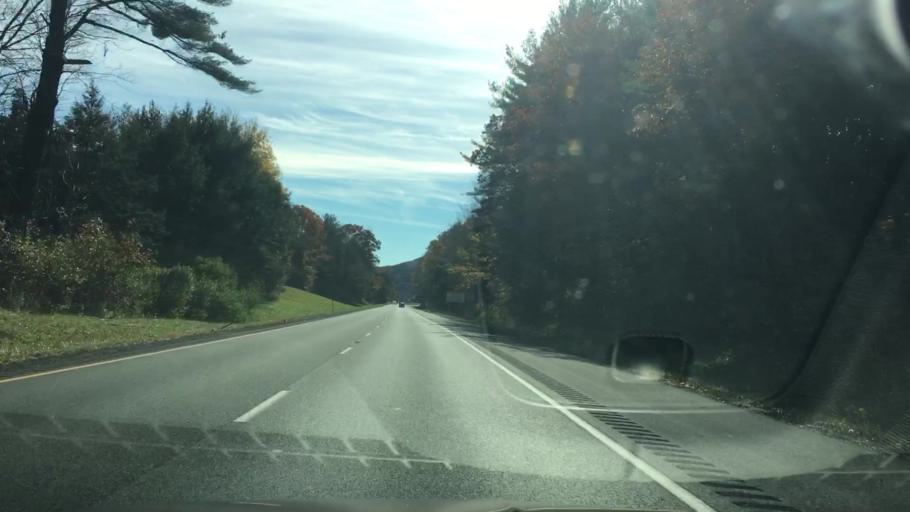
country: US
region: Massachusetts
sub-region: Franklin County
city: Bernardston
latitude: 42.7248
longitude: -72.5697
